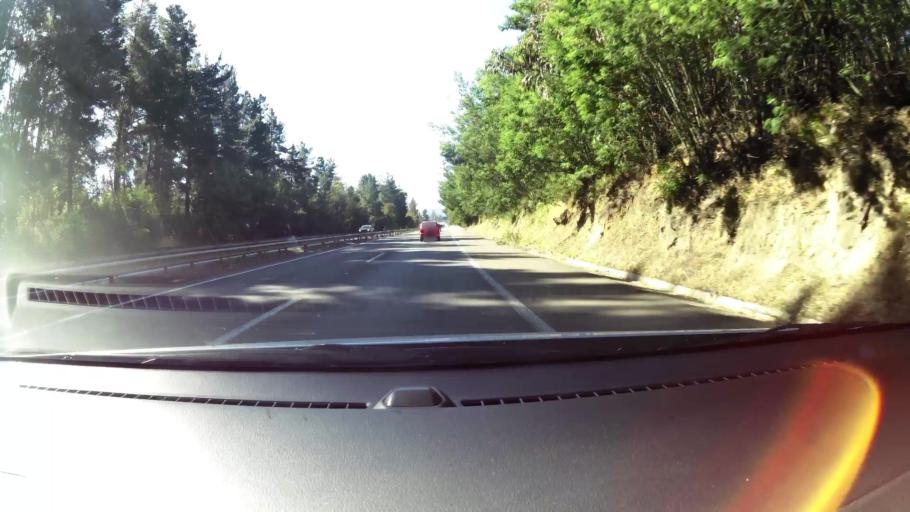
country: CL
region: Valparaiso
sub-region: Provincia de Valparaiso
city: Vina del Mar
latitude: -33.1518
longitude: -71.5574
